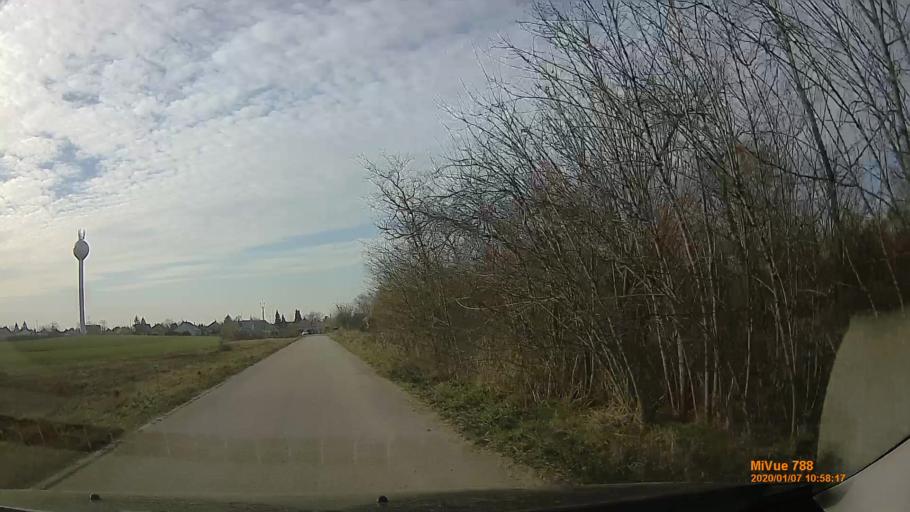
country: HU
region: Gyor-Moson-Sopron
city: Rajka
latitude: 47.9148
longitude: 17.1697
